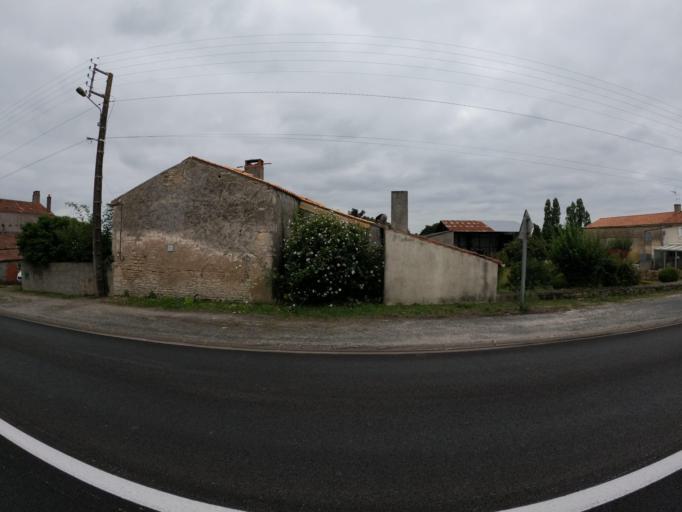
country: FR
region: Pays de la Loire
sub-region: Departement de la Vendee
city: Saint-Martin-sous-Mouzeuil
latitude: 46.5102
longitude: -0.9562
